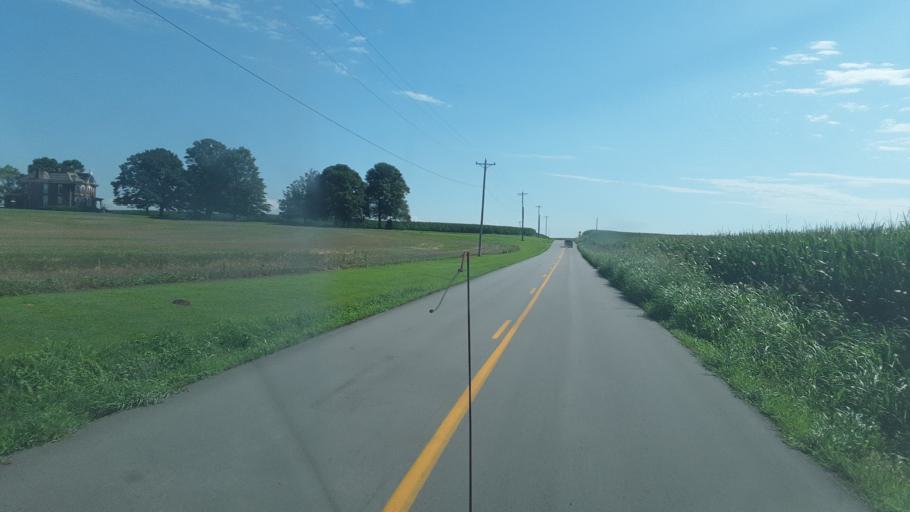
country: US
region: Kentucky
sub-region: Todd County
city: Elkton
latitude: 36.7438
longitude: -87.2294
